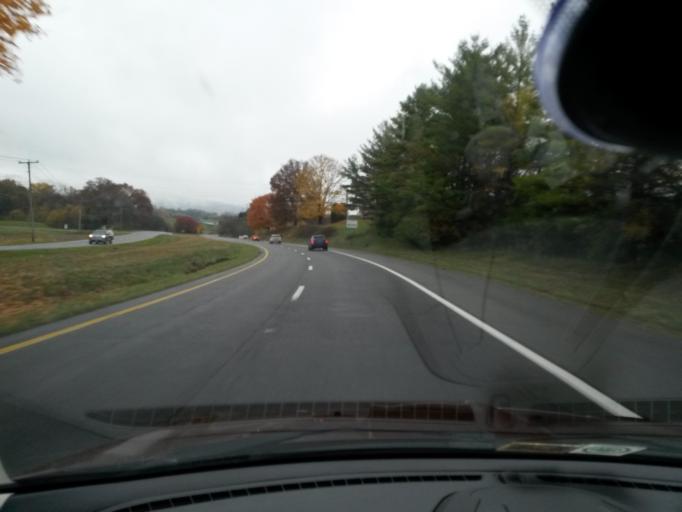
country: US
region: Virginia
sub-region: Botetourt County
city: Fincastle
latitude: 37.4827
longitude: -79.8781
